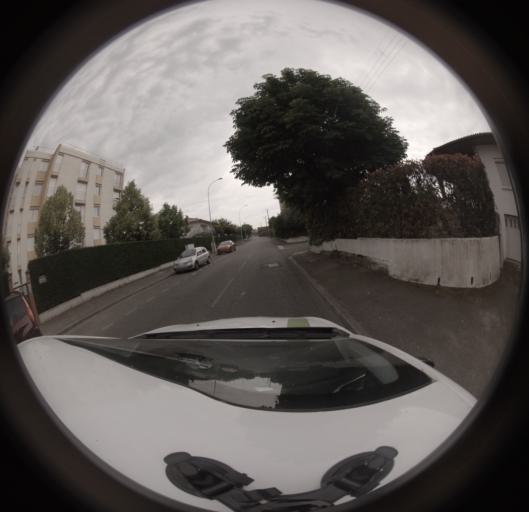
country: FR
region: Midi-Pyrenees
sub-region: Departement du Tarn-et-Garonne
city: Montauban
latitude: 44.0147
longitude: 1.3750
